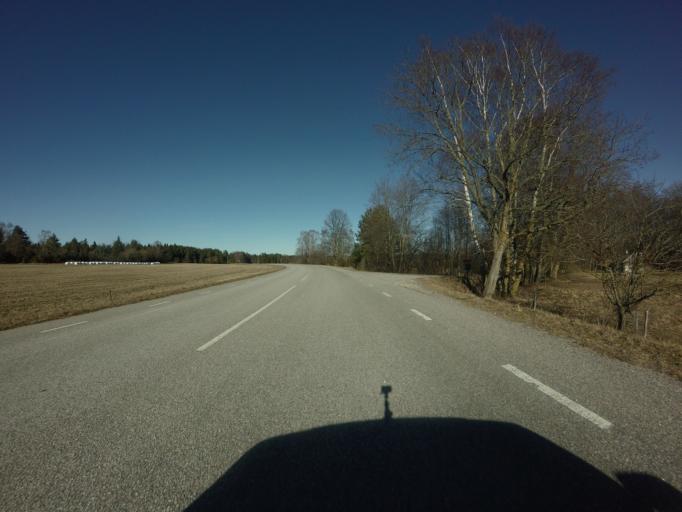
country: EE
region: Saare
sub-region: Kuressaare linn
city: Kuressaare
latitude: 58.4757
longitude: 22.2304
